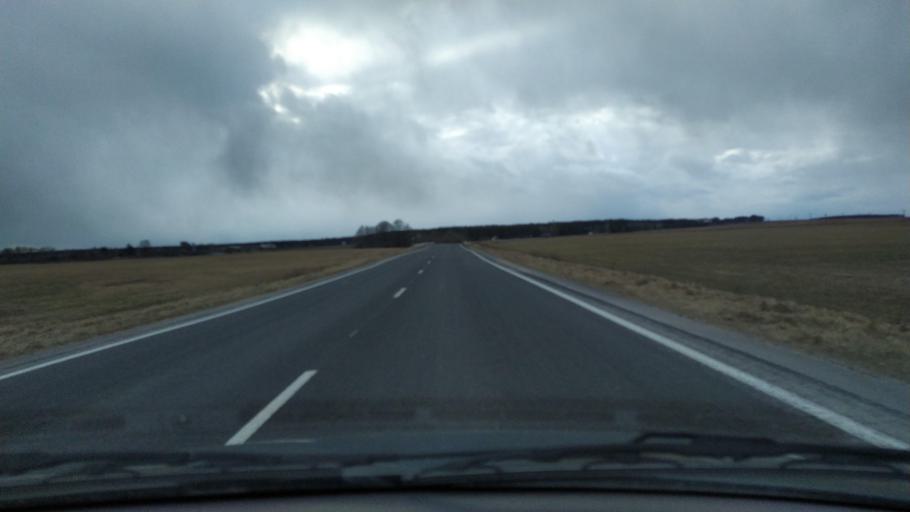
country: BY
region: Brest
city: Kamyanyets
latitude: 52.4005
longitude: 23.8957
